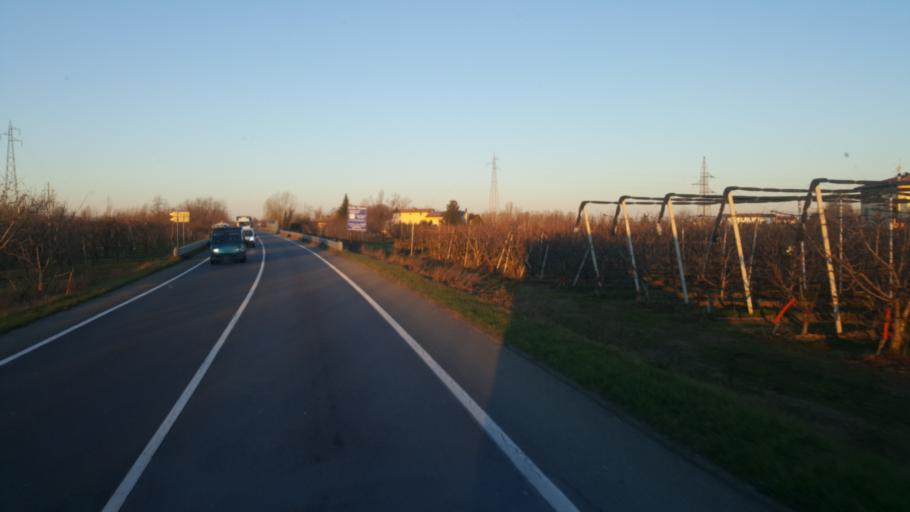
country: IT
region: Emilia-Romagna
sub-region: Provincia di Modena
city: Mulino
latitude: 44.5053
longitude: 11.0468
